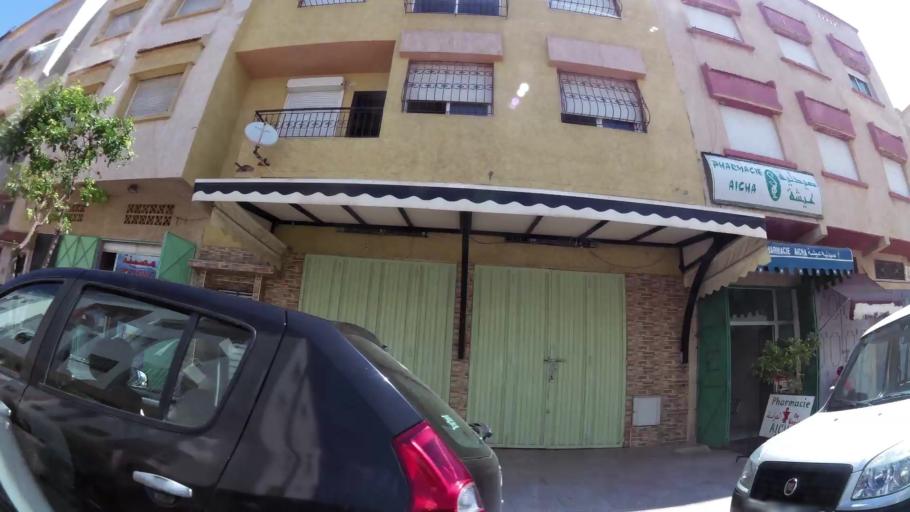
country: MA
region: Rabat-Sale-Zemmour-Zaer
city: Sale
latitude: 34.0744
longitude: -6.7870
